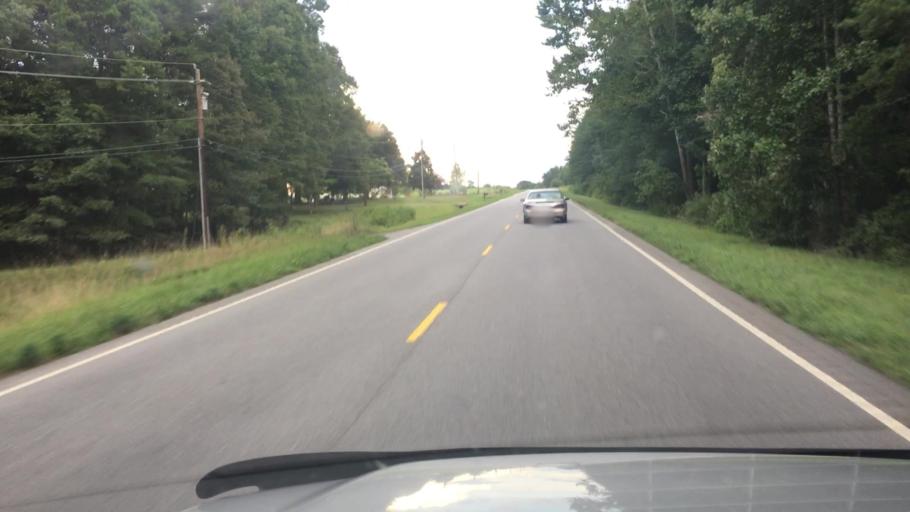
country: US
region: South Carolina
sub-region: Spartanburg County
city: Mayo
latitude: 35.1353
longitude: -81.8037
